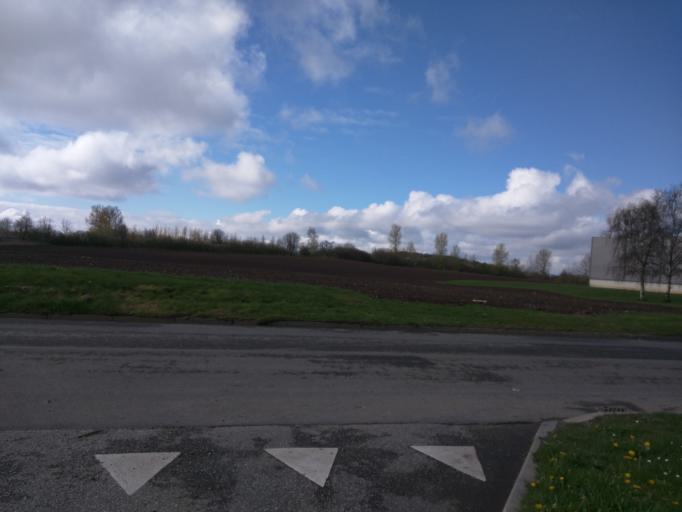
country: DK
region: South Denmark
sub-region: Fredericia Kommune
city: Snoghoj
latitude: 55.5385
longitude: 9.6987
